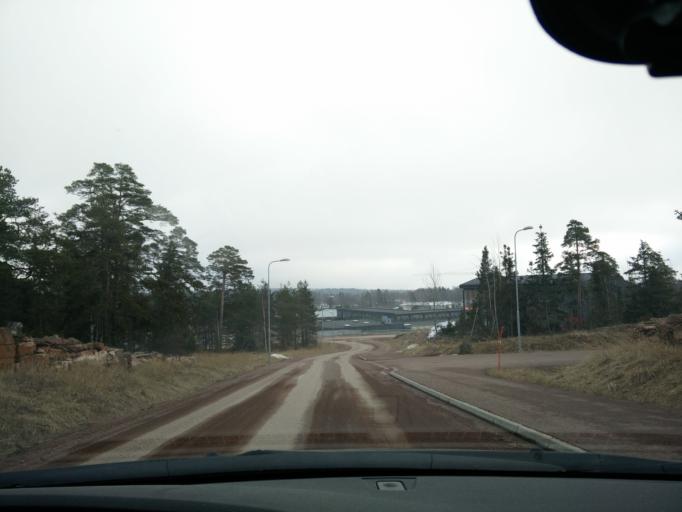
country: AX
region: Alands landsbygd
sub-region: Jomala
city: Jomala
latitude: 60.1321
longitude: 19.9310
